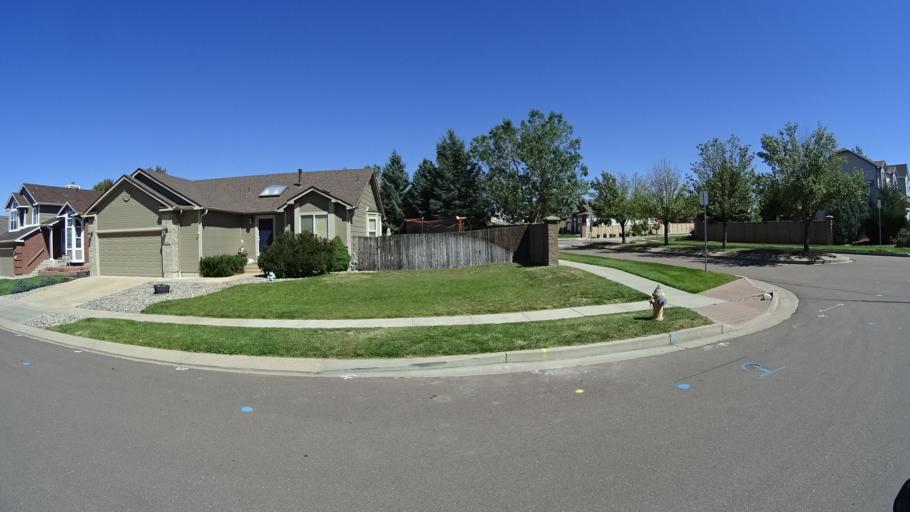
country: US
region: Colorado
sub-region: El Paso County
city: Security-Widefield
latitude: 38.7863
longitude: -104.7339
